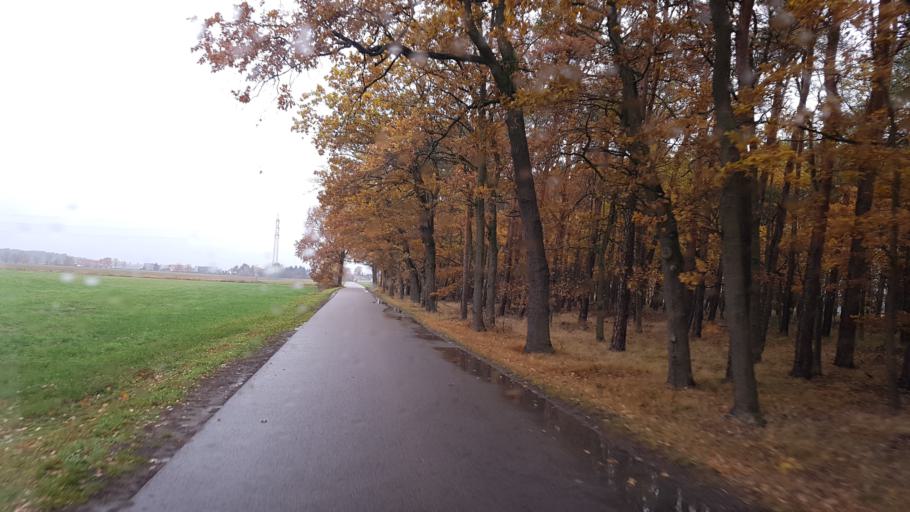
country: DE
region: Brandenburg
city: Herzberg
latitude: 51.6501
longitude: 13.2331
